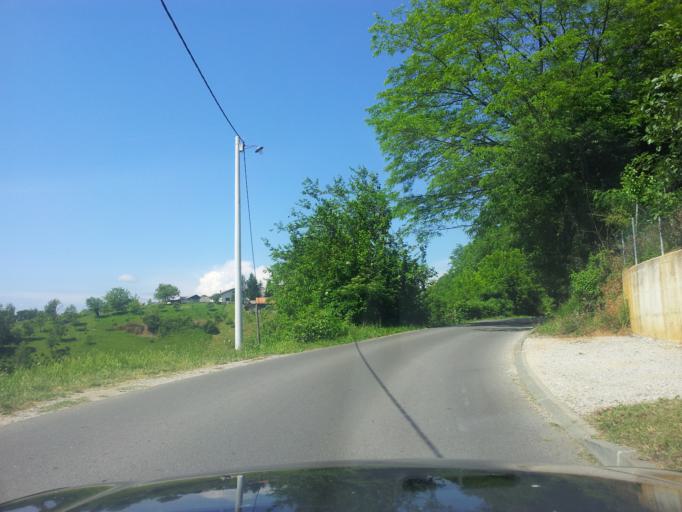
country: HR
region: Karlovacka
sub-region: Grad Karlovac
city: Karlovac
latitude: 45.4825
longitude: 15.4837
